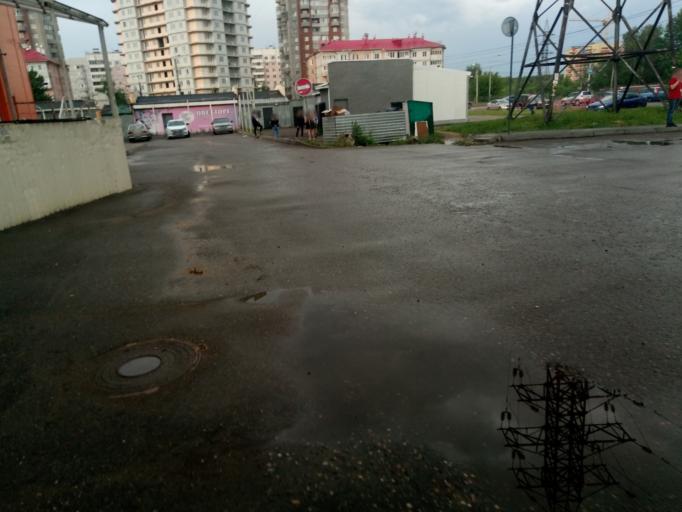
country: RU
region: Jaroslavl
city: Yaroslavl
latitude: 57.6448
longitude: 39.9539
